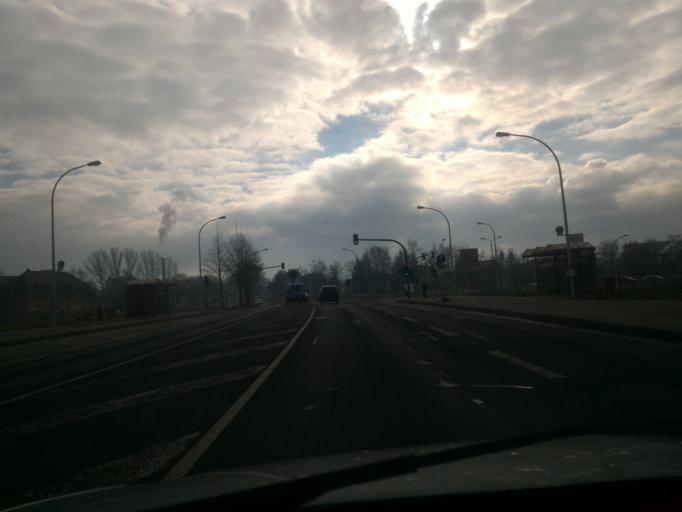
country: DE
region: Saxony
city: Zittau
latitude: 50.8911
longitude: 14.8115
